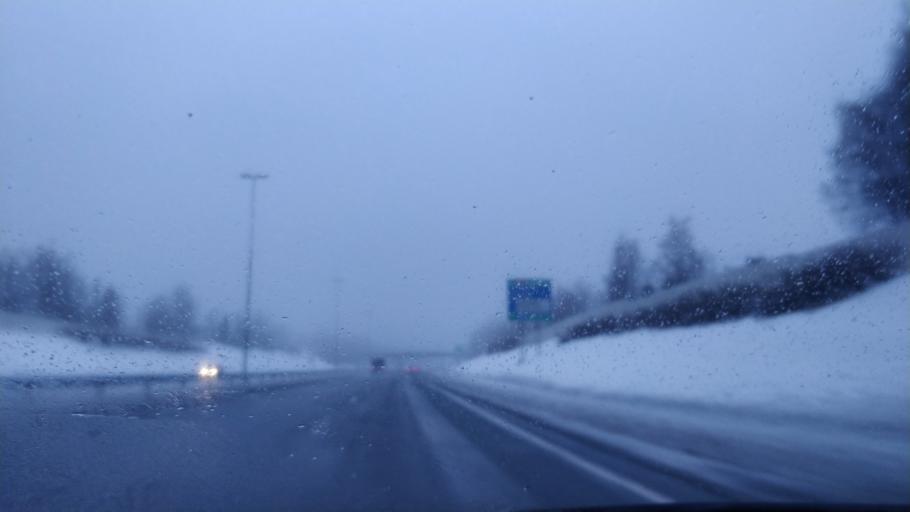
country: FI
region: Lapland
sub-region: Kemi-Tornio
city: Kemi
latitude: 65.7482
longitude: 24.5778
